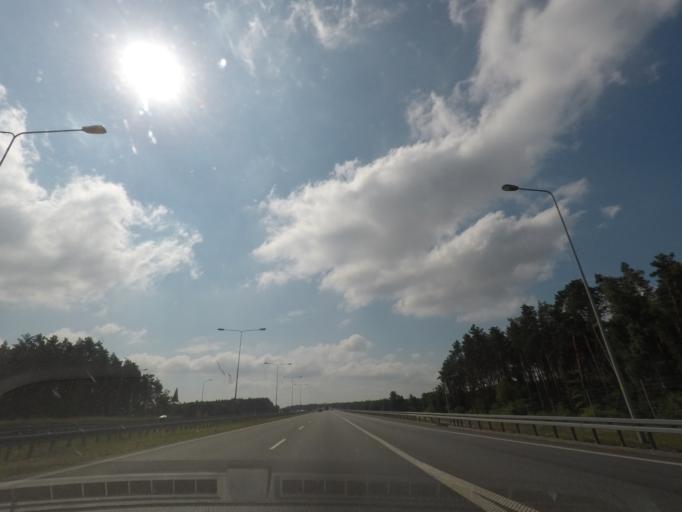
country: PL
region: Kujawsko-Pomorskie
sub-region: Powiat aleksandrowski
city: Aleksandrow Kujawski
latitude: 52.8991
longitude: 18.7238
